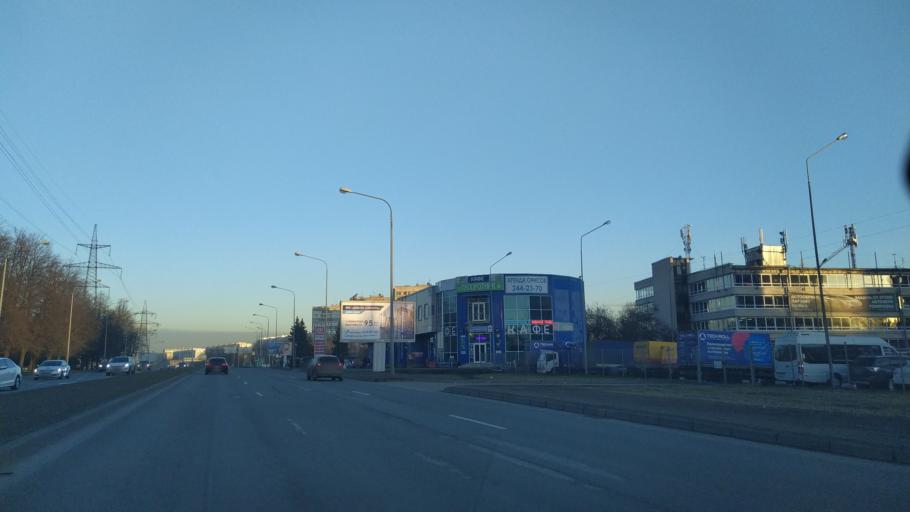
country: RU
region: Leningrad
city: Kalininskiy
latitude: 59.9754
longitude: 30.4111
